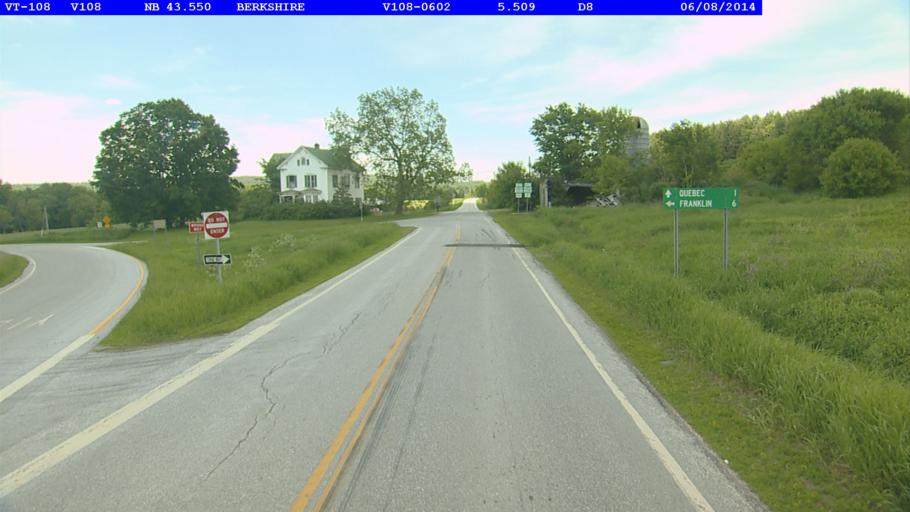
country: US
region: Vermont
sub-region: Franklin County
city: Enosburg Falls
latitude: 44.9969
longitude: -72.8223
